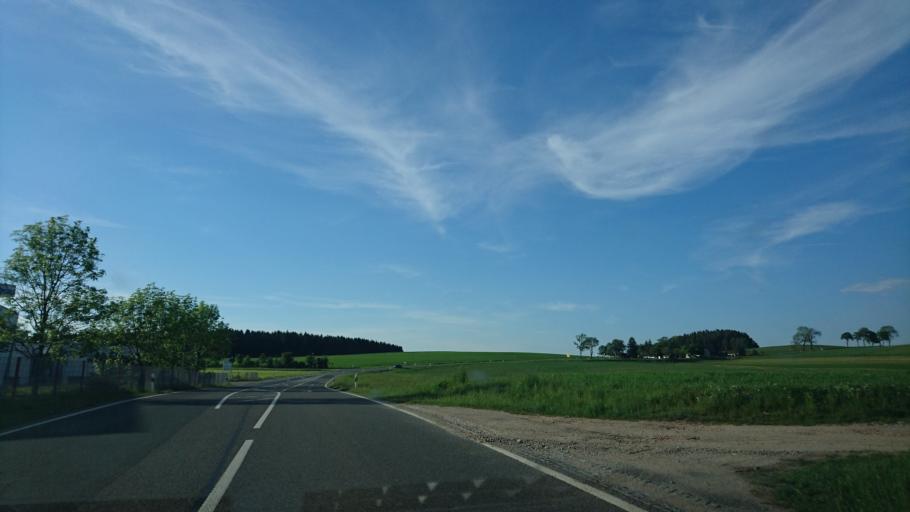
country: DE
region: Saxony
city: Stutzengrun
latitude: 50.5375
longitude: 12.5321
